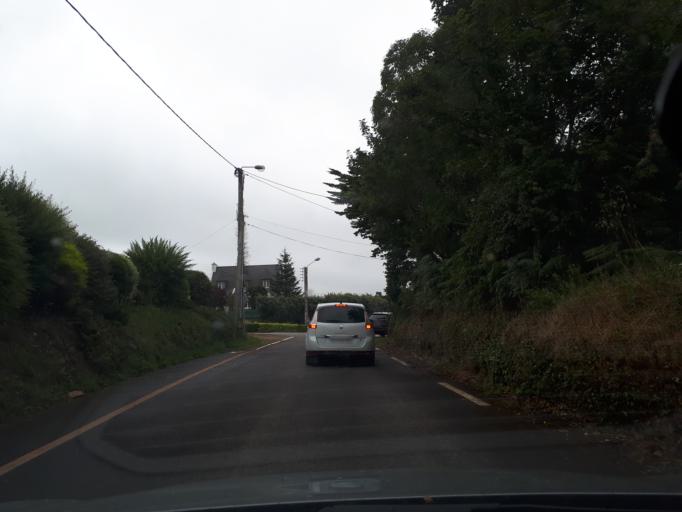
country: FR
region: Brittany
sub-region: Departement du Finistere
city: Carantec
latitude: 48.6573
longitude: -3.9205
